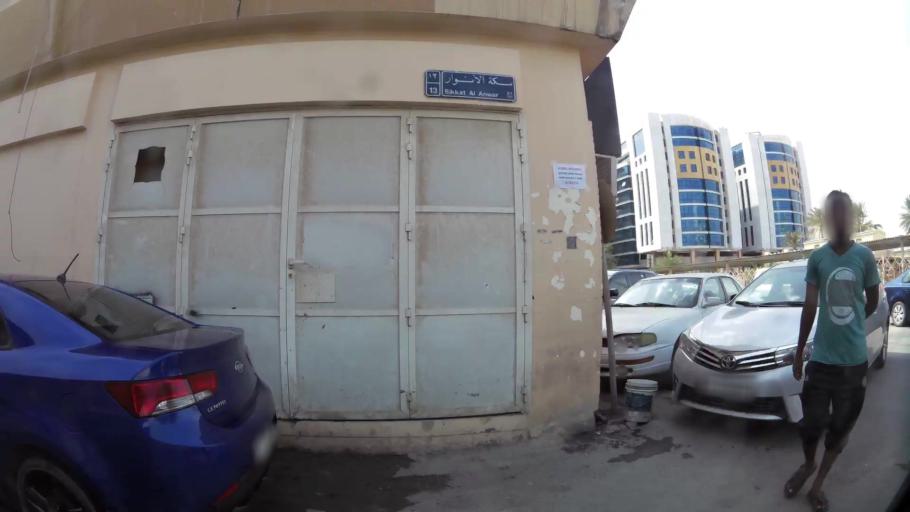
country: QA
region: Baladiyat ad Dawhah
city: Doha
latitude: 25.2821
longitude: 51.5228
